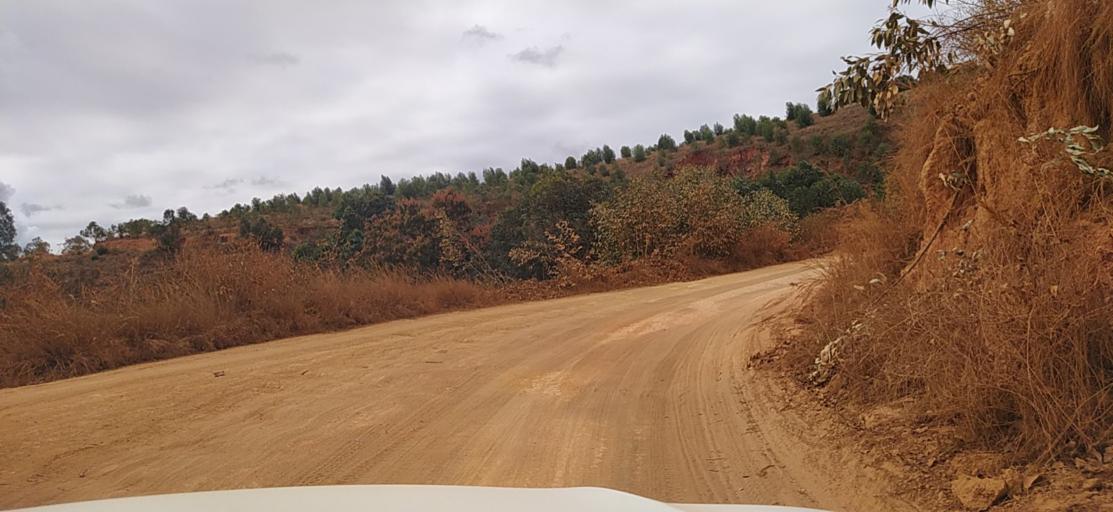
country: MG
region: Alaotra Mangoro
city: Ambatondrazaka
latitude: -17.9991
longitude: 48.2623
